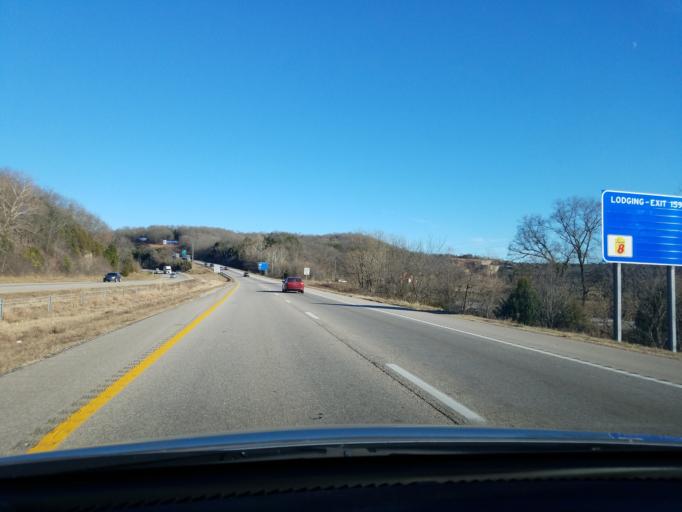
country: US
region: Missouri
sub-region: Pulaski County
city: Waynesville
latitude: 37.8174
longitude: -92.1914
